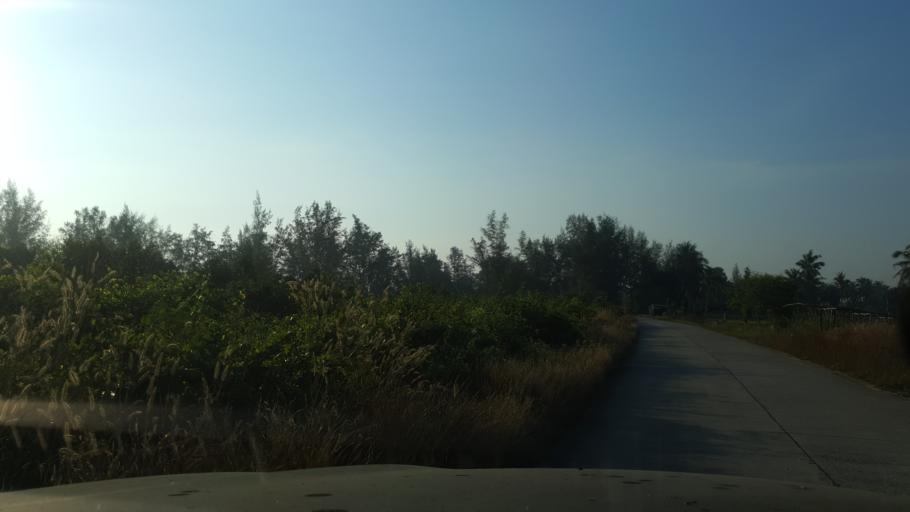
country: TH
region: Prachuap Khiri Khan
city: Bang Saphan
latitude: 11.2889
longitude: 99.5489
